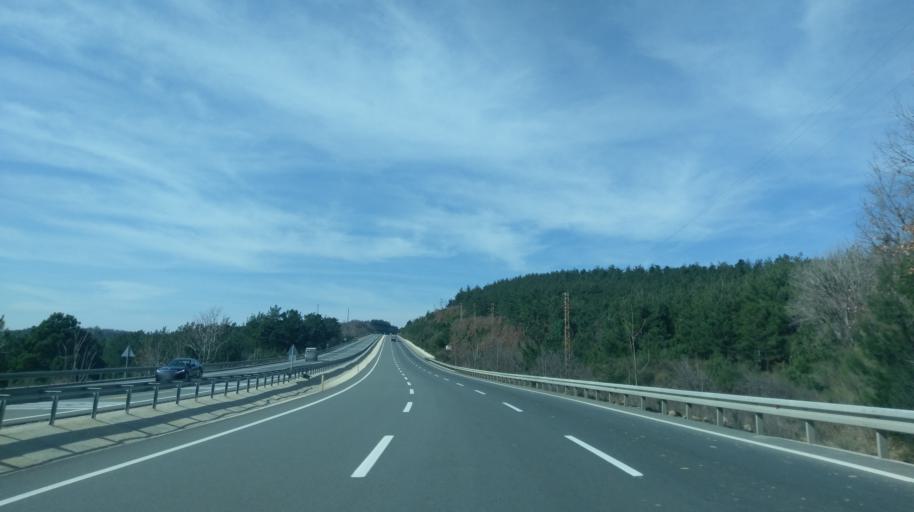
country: TR
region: Canakkale
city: Evrese
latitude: 40.7079
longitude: 26.7819
